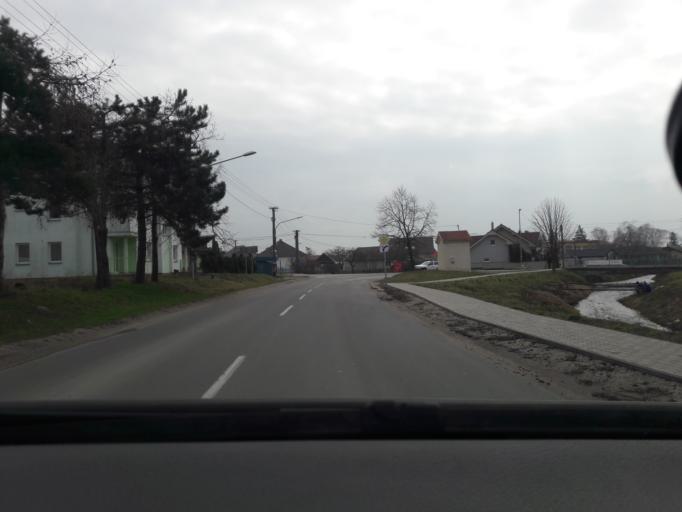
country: SK
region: Trnavsky
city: Smolenice
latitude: 48.4672
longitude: 17.4419
